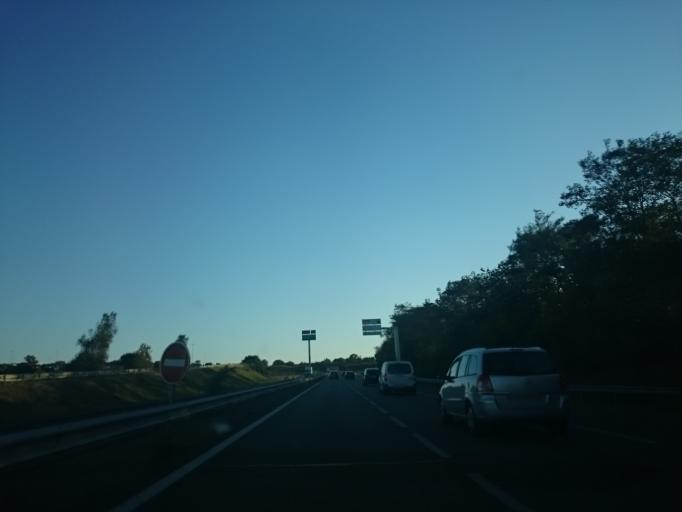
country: FR
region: Brittany
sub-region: Departement d'Ille-et-Vilaine
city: Bain-de-Bretagne
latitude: 47.8541
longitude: -1.6932
